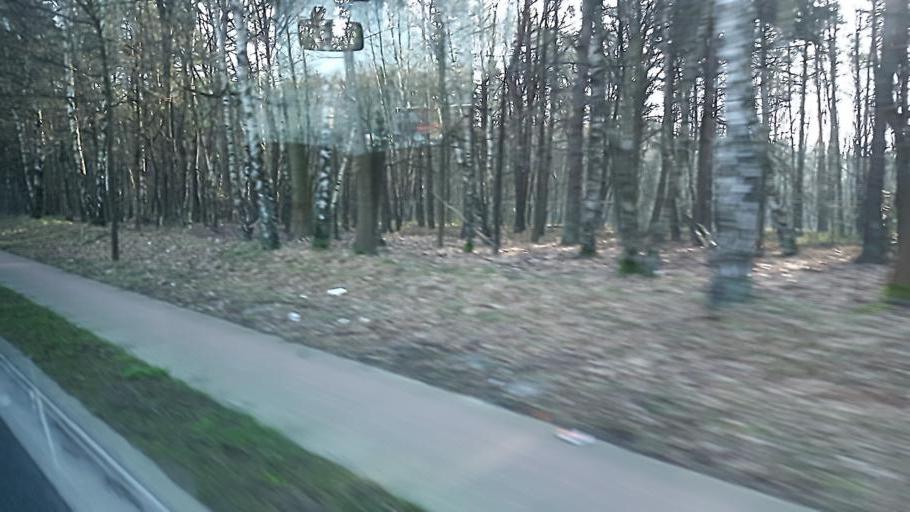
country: BE
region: Flanders
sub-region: Provincie Limburg
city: Genk
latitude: 51.0035
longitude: 5.4782
